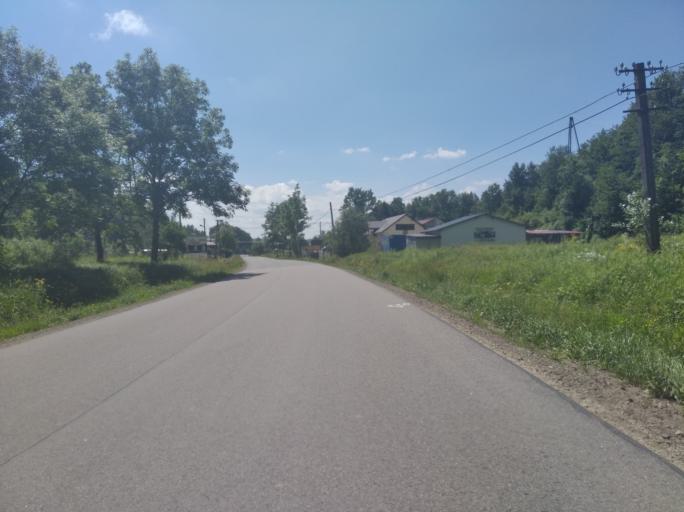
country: PL
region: Subcarpathian Voivodeship
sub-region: Powiat brzozowski
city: Grabownica Starzenska
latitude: 49.6698
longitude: 22.0841
